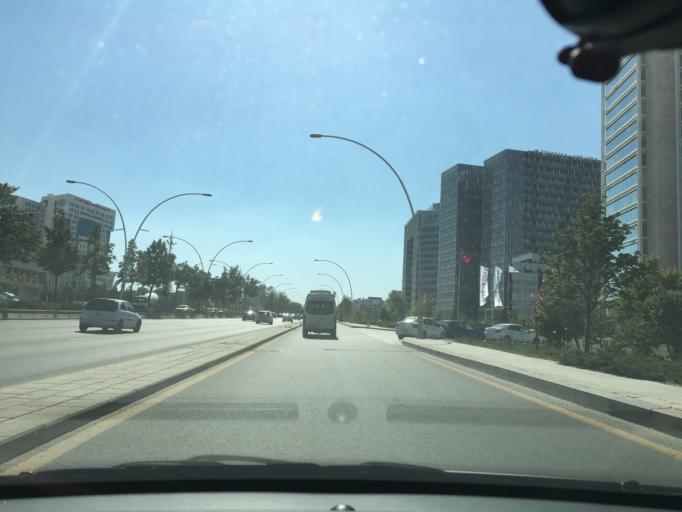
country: TR
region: Ankara
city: Batikent
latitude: 39.9077
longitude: 32.7565
